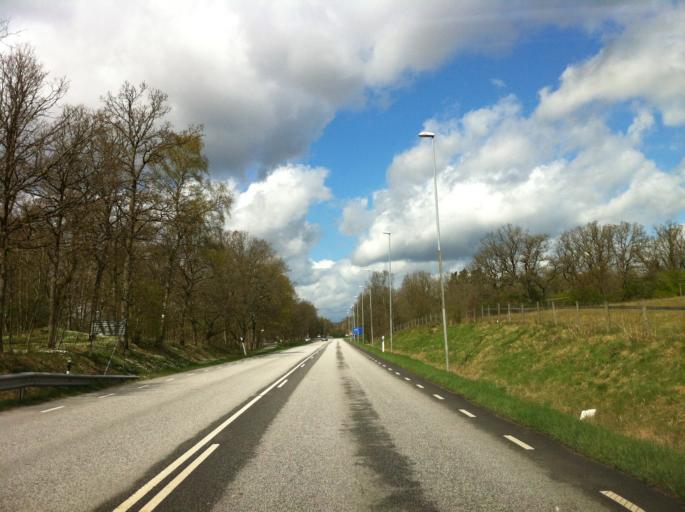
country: SE
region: Skane
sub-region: Hoors Kommun
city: Satofta
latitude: 55.9331
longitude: 13.5594
